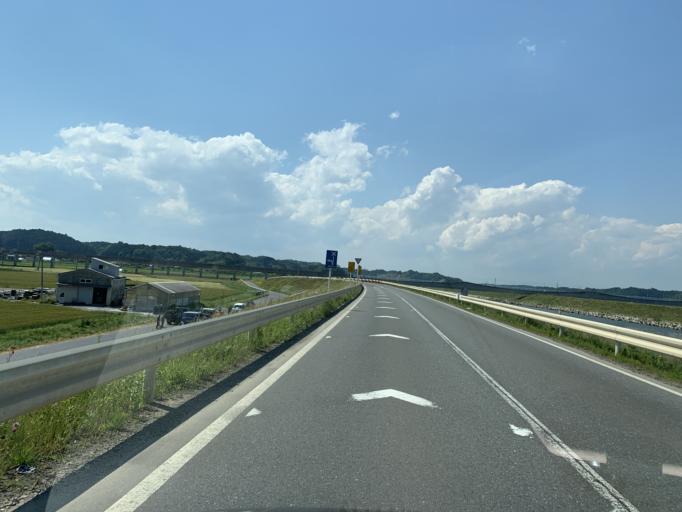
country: JP
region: Miyagi
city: Yamoto
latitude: 38.3857
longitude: 141.1659
